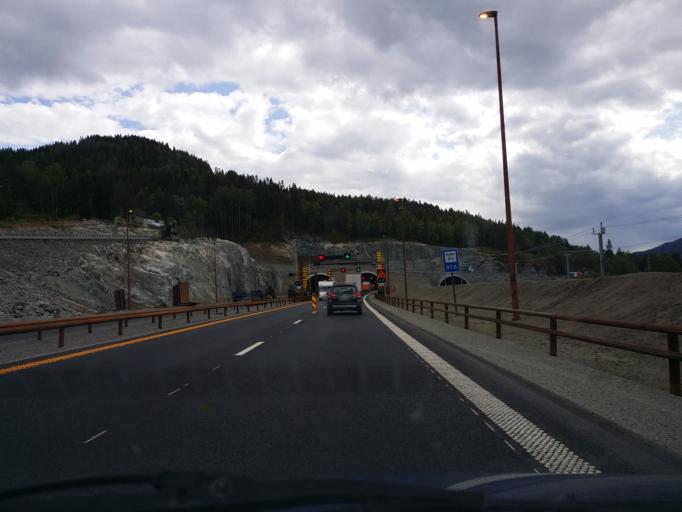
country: NO
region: Akershus
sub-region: Eidsvoll
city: Eidsvoll
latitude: 60.4414
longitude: 11.2419
